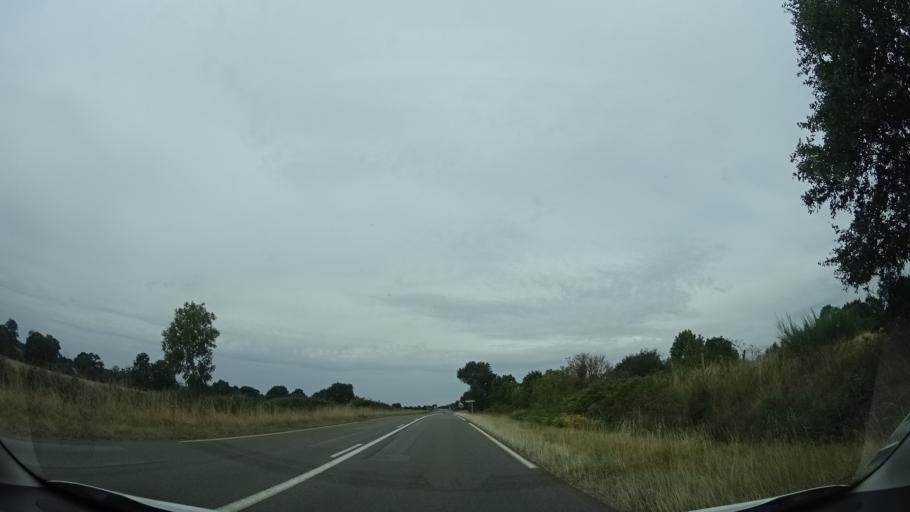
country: FR
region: Pays de la Loire
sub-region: Departement de la Mayenne
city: Meslay-du-Maine
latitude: 47.9417
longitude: -0.5175
